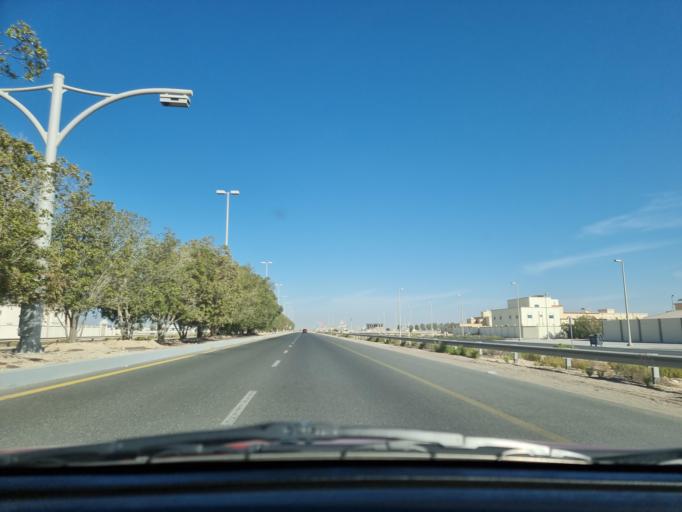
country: AE
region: Abu Dhabi
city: Abu Dhabi
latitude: 24.3945
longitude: 54.6941
